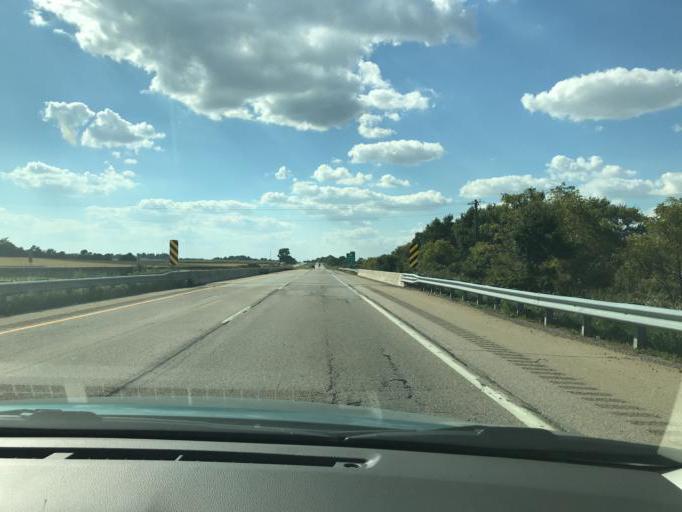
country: US
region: Wisconsin
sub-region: Rock County
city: Clinton
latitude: 42.5725
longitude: -88.8341
